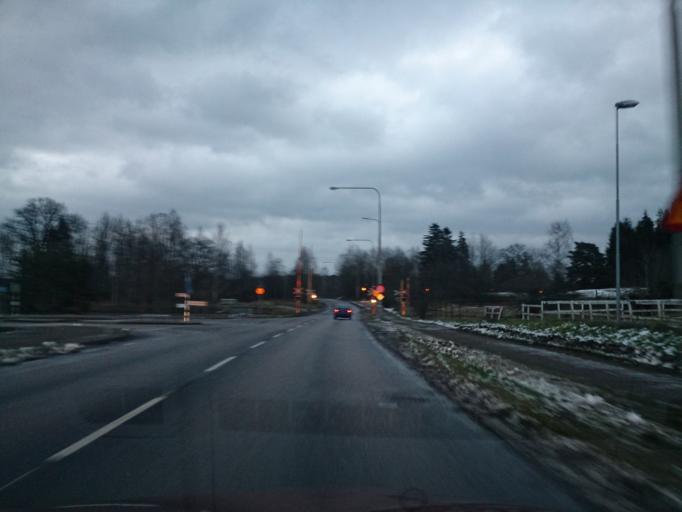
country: SE
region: OEstergoetland
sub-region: Linkopings Kommun
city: Sturefors
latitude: 58.3766
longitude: 15.7158
